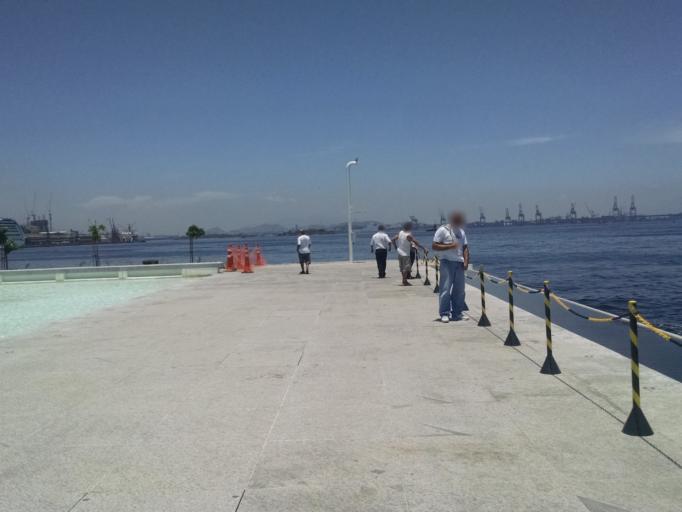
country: BR
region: Rio de Janeiro
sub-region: Rio De Janeiro
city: Rio de Janeiro
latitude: -22.8925
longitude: -43.1788
